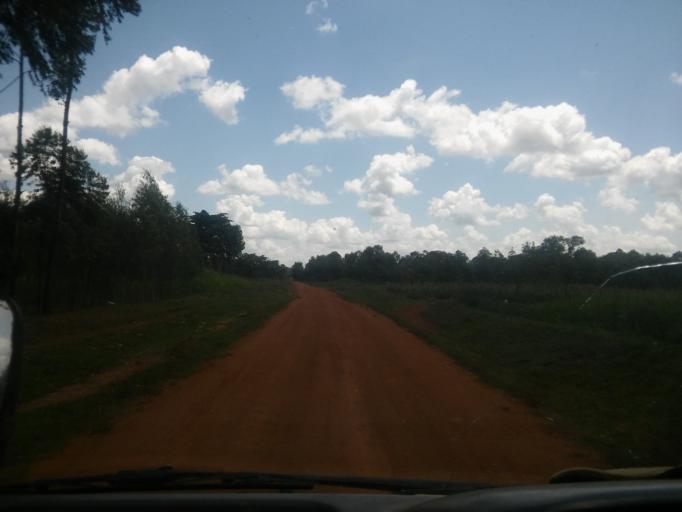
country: UG
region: Eastern Region
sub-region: Budaka District
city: Budaka
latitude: 1.1110
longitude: 33.9630
